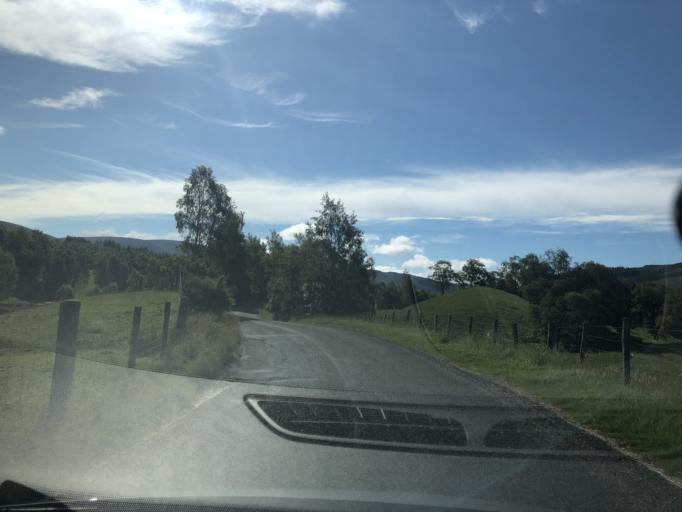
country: GB
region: Scotland
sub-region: Angus
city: Kirriemuir
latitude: 56.8405
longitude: -3.0925
